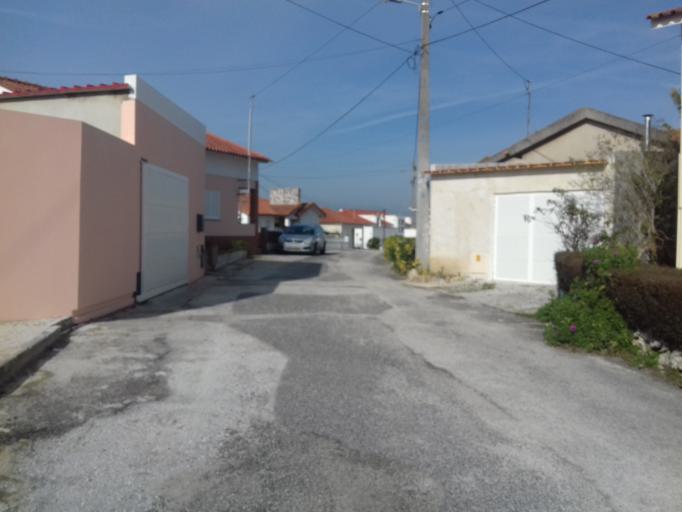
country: PT
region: Leiria
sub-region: Porto de Mos
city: Porto de Mos
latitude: 39.6016
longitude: -8.8129
